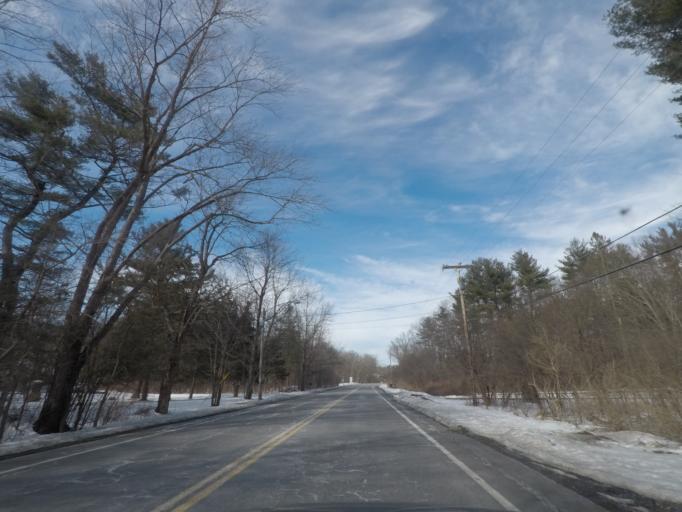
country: US
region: New York
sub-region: Albany County
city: Voorheesville
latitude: 42.6555
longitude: -73.9391
